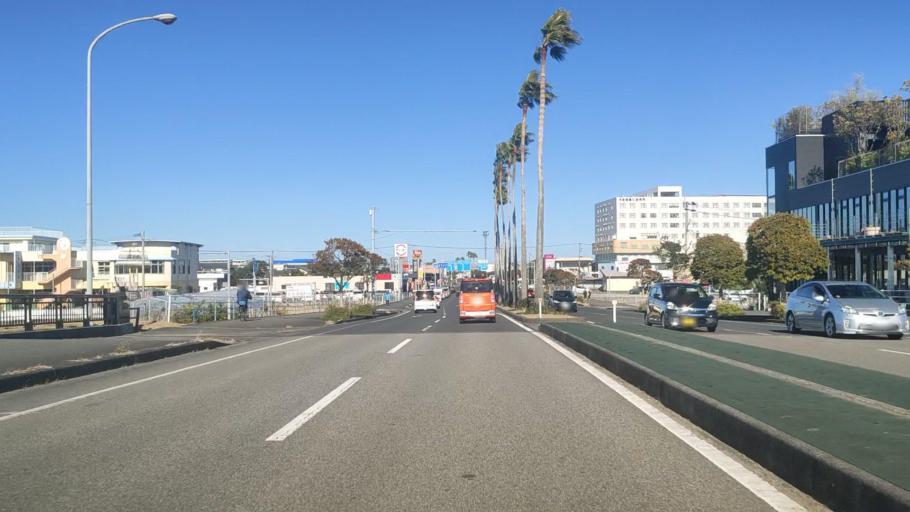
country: JP
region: Miyazaki
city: Miyazaki-shi
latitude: 31.9198
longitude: 131.4511
